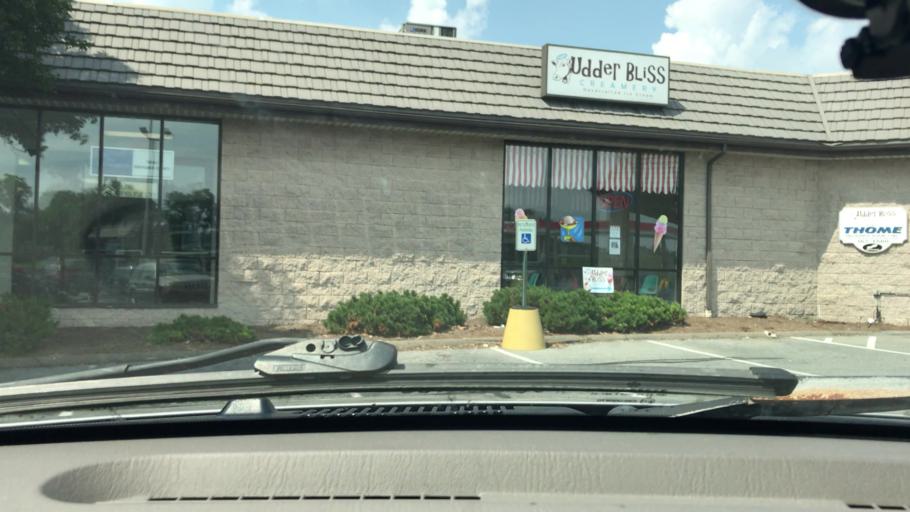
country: US
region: Pennsylvania
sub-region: Lancaster County
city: Elizabethtown
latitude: 40.1626
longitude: -76.5732
